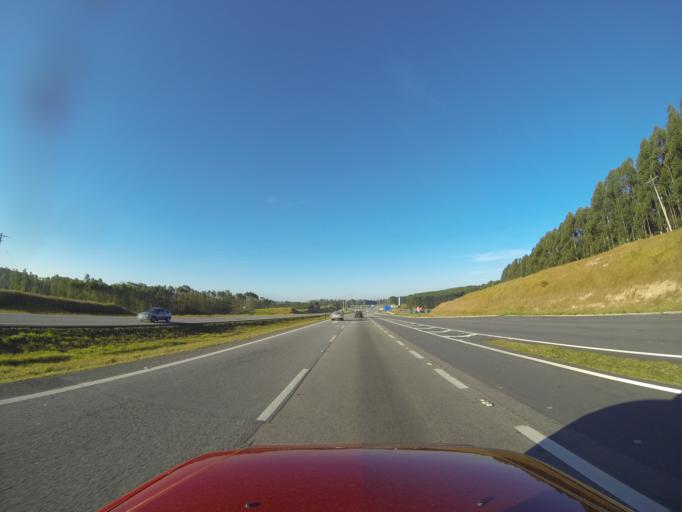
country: BR
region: Sao Paulo
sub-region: Jacarei
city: Jacarei
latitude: -23.2883
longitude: -45.8666
